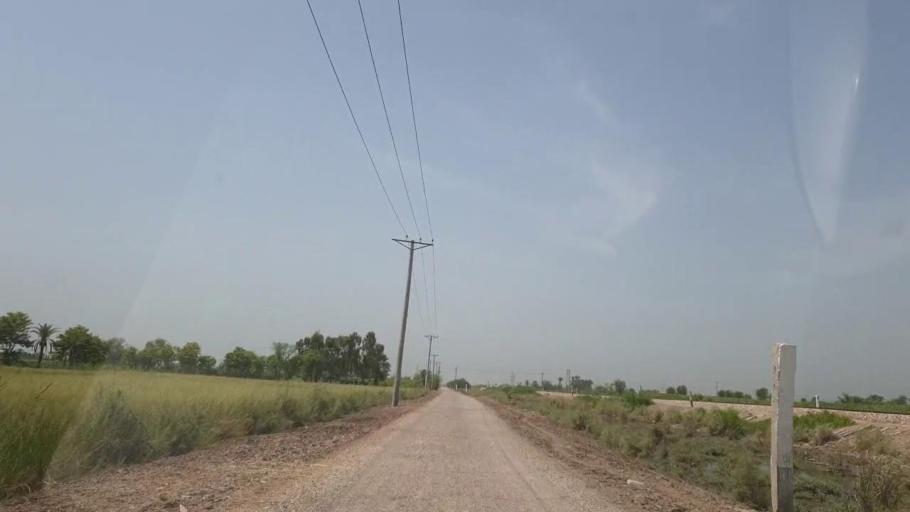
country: PK
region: Sindh
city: Gambat
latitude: 27.3223
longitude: 68.5373
